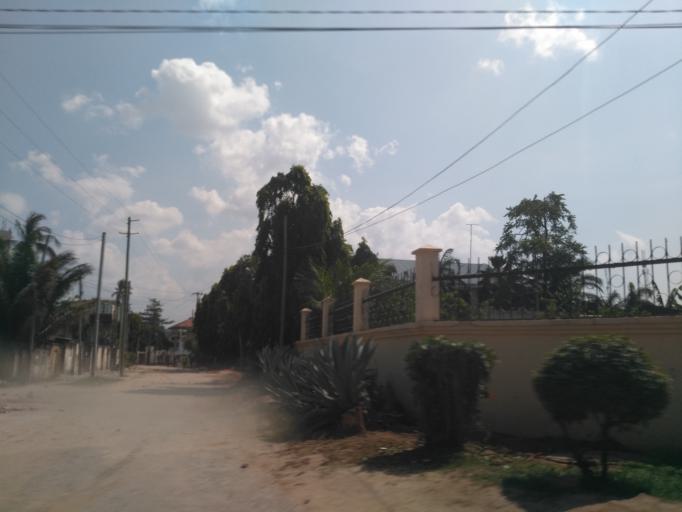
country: TZ
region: Dar es Salaam
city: Dar es Salaam
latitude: -6.8014
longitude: 39.2830
